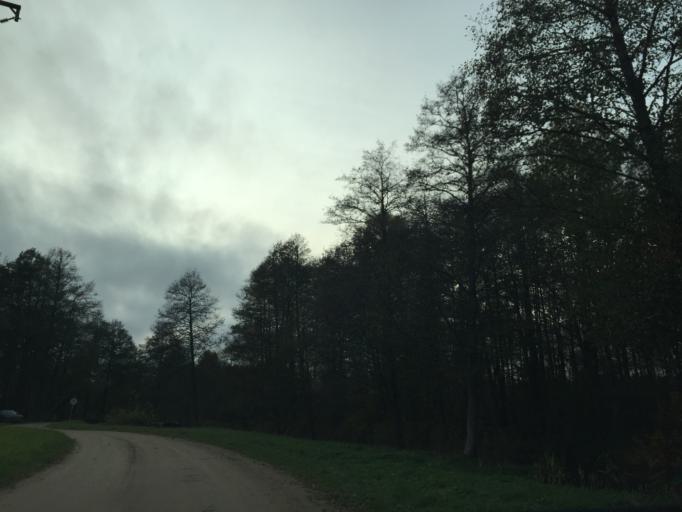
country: LV
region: Cesu Rajons
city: Cesis
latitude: 57.3228
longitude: 25.1511
